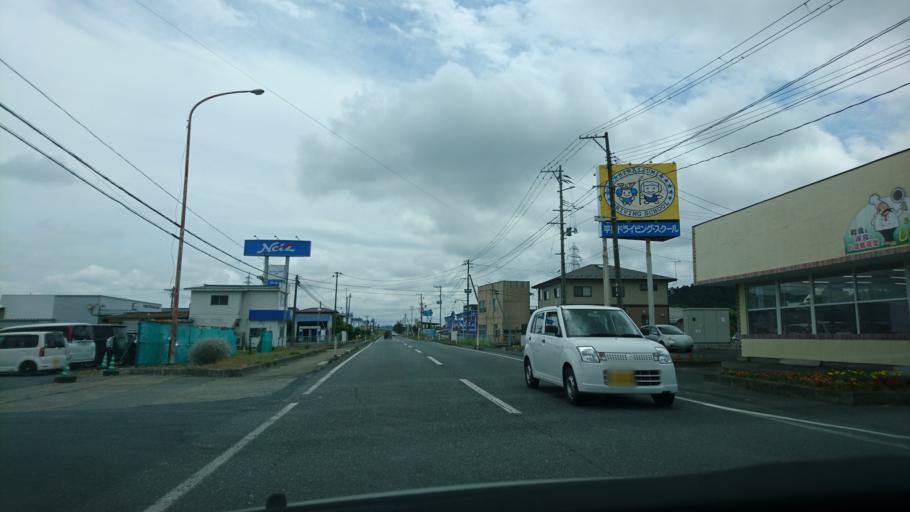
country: JP
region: Iwate
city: Ichinoseki
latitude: 38.9655
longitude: 141.1236
